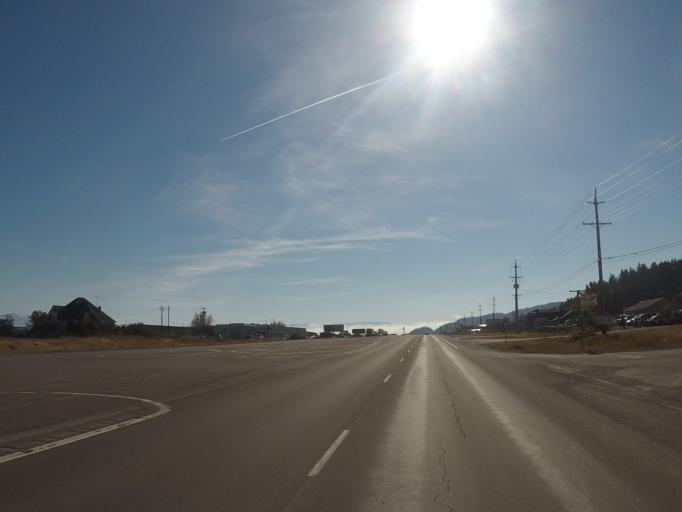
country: US
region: Montana
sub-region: Flathead County
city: Somers
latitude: 48.1249
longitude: -114.2619
